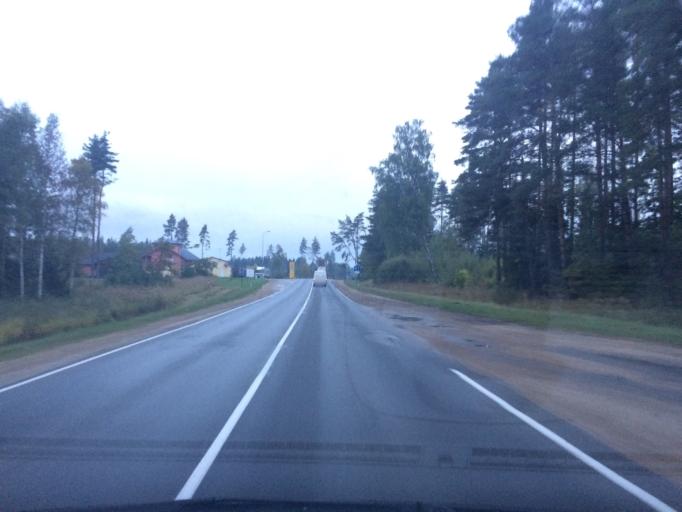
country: LV
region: Jekabpils Rajons
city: Jekabpils
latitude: 56.5333
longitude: 25.8205
